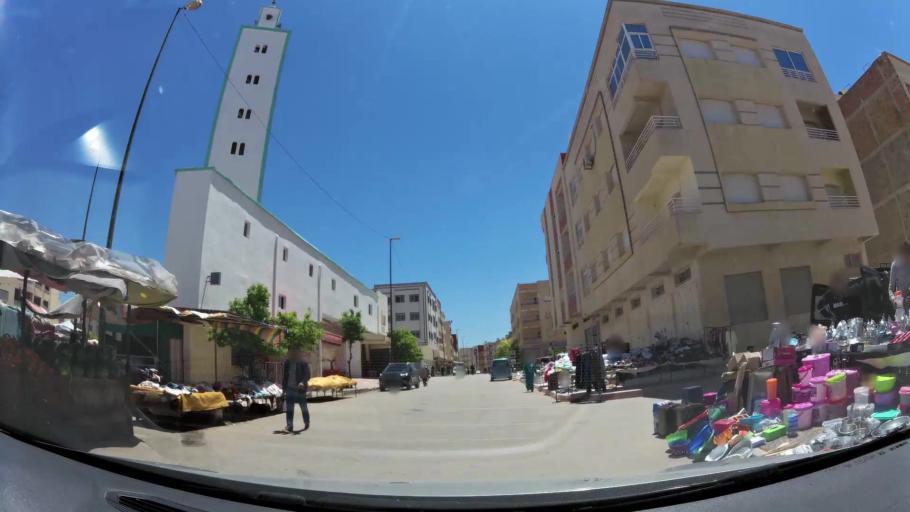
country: MA
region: Meknes-Tafilalet
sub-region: Meknes
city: Meknes
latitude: 33.8634
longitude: -5.5673
